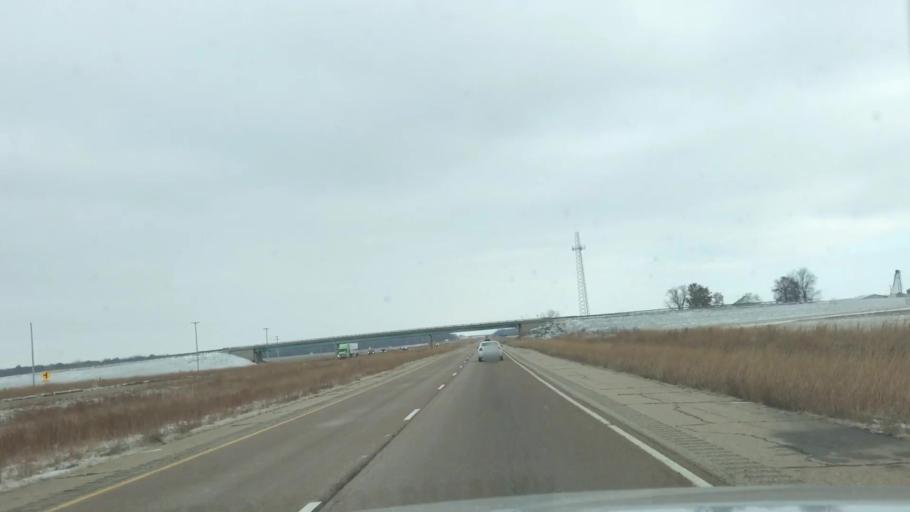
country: US
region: Illinois
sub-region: Montgomery County
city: Raymond
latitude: 39.4184
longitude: -89.6433
